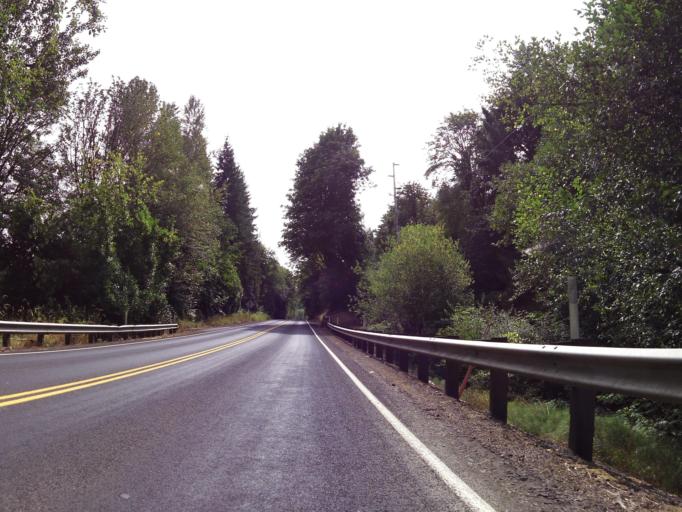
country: US
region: Washington
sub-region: Cowlitz County
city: Castle Rock
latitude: 46.3530
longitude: -122.9381
